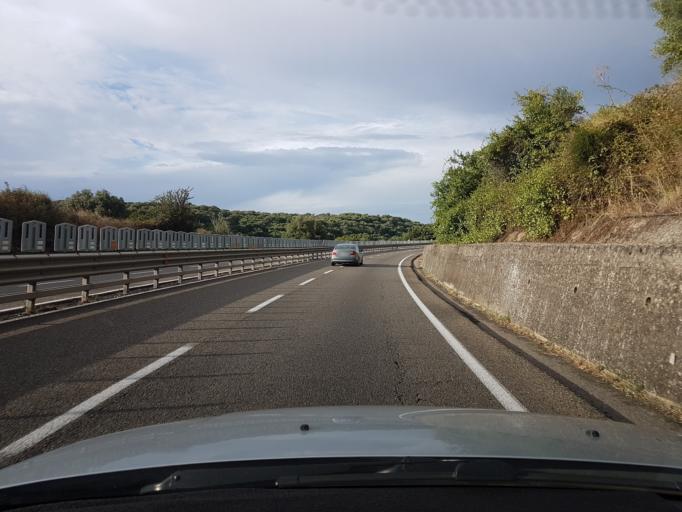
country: IT
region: Sardinia
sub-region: Provincia di Oristano
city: Bauladu
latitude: 40.0504
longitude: 8.7089
